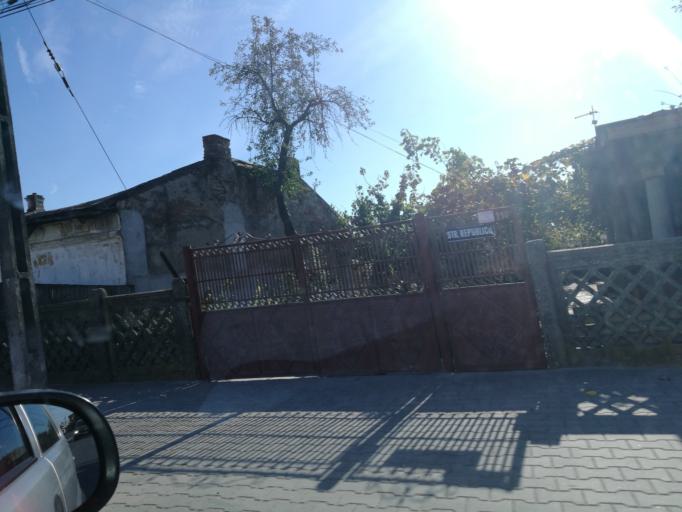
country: RO
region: Ilfov
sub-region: Comuna Dragomiresti-Vale
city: Dragomiresti-Deal
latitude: 44.4564
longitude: 25.9510
